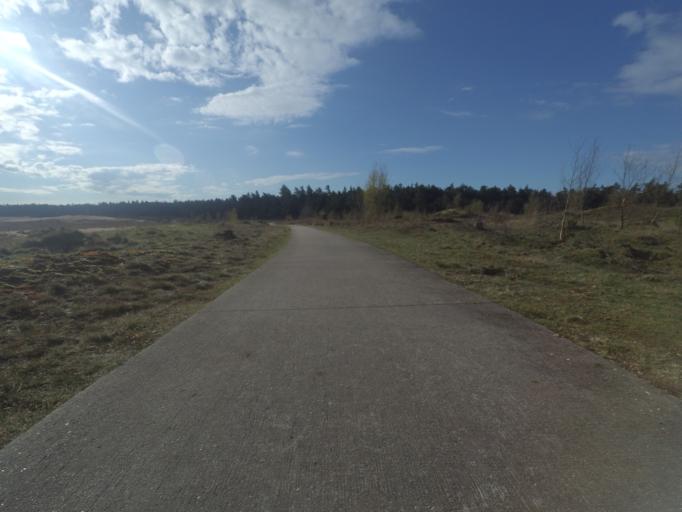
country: NL
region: Gelderland
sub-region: Gemeente Ede
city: Otterlo
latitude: 52.1523
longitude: 5.8510
